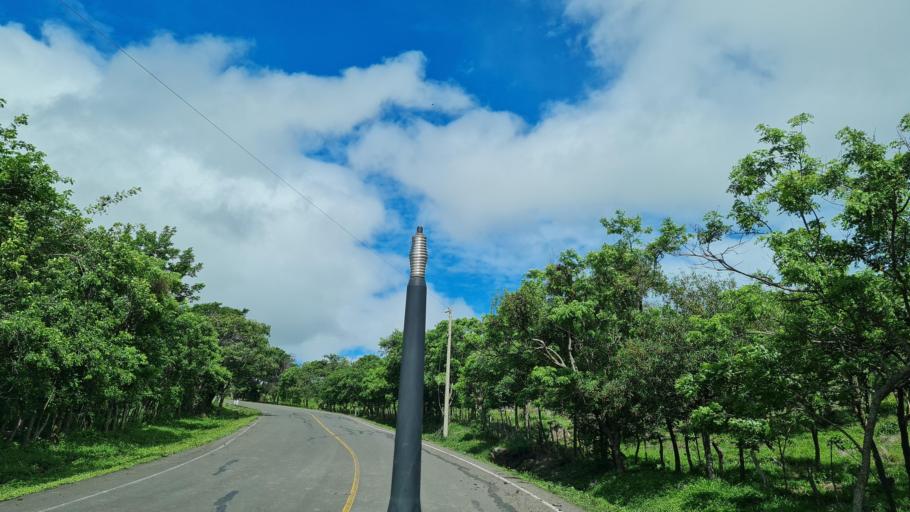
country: NI
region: Boaco
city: San Jose de los Remates
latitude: 12.6169
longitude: -85.8675
